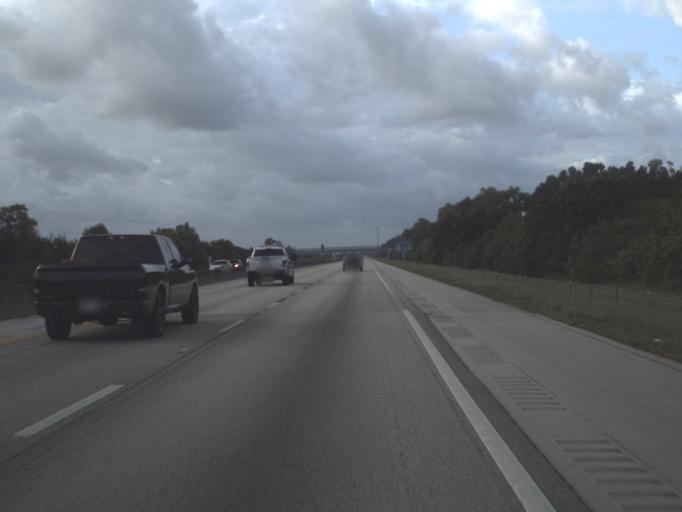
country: US
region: Florida
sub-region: Palm Beach County
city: Schall Circle
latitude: 26.7433
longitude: -80.1348
